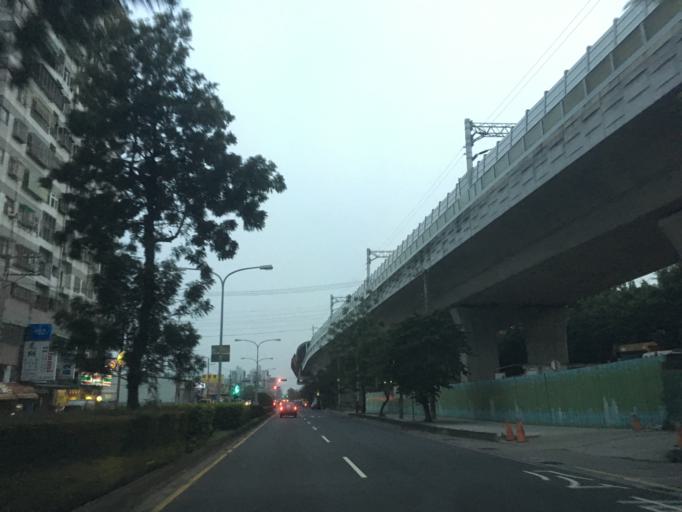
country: TW
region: Taiwan
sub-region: Taichung City
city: Taichung
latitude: 24.1667
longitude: 120.7004
